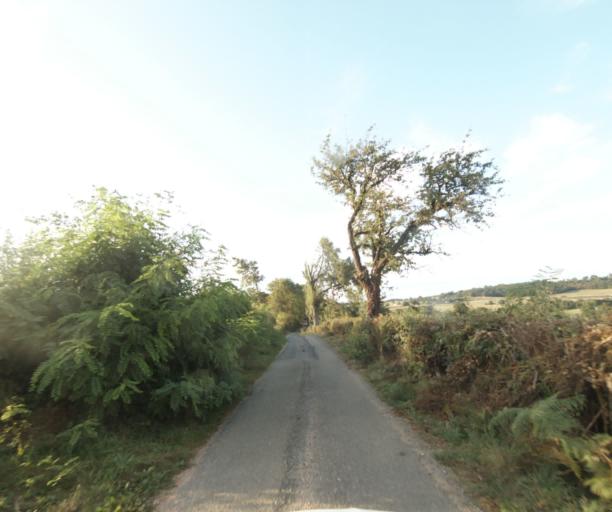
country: FR
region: Bourgogne
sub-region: Departement de Saone-et-Loire
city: Charolles
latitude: 46.4408
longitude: 4.3625
